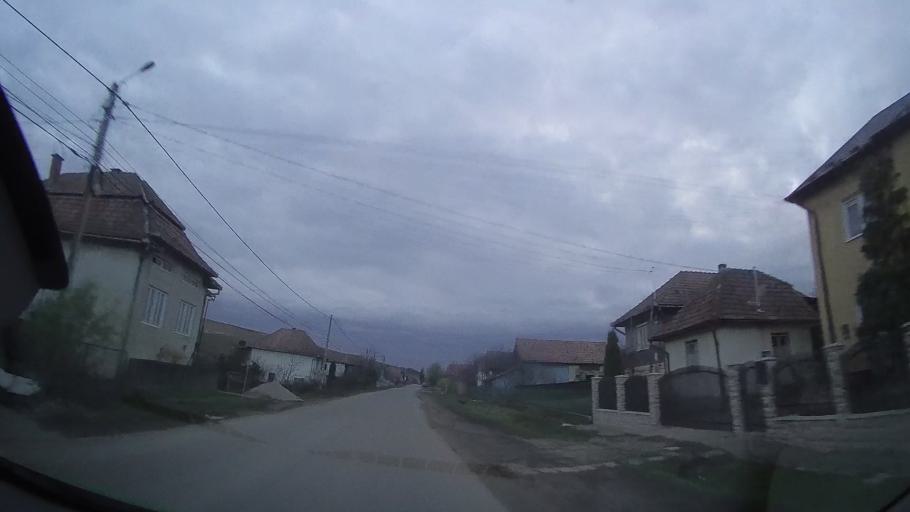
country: RO
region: Cluj
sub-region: Comuna Caianu
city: Vaida-Camaras
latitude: 46.8261
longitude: 23.9435
